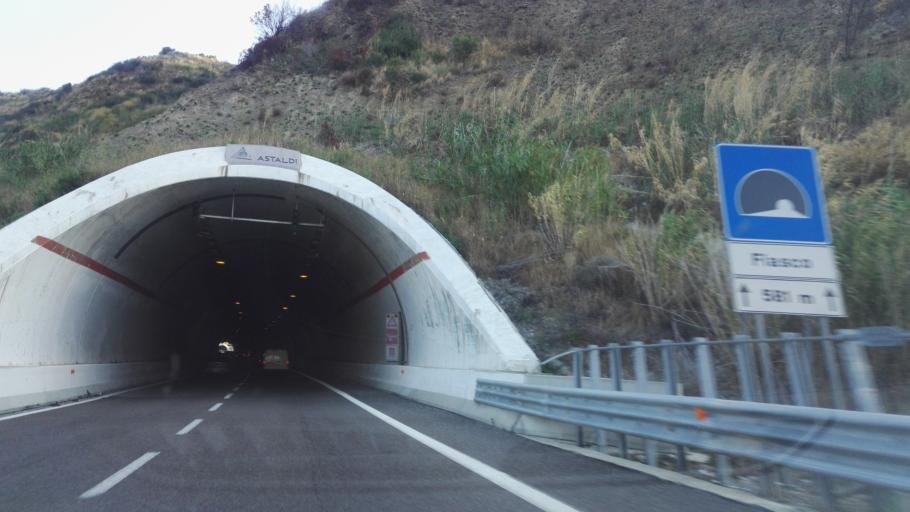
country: IT
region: Calabria
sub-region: Provincia di Catanzaro
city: Squillace Lido
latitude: 38.8048
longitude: 16.5564
